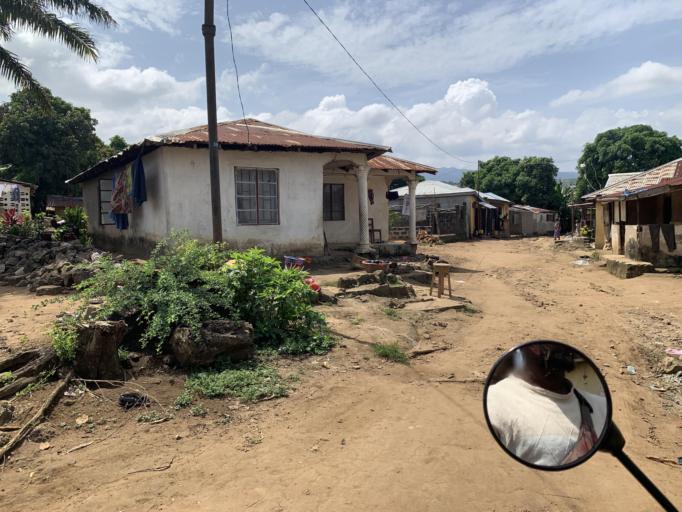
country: SL
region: Western Area
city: Hastings
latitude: 8.4104
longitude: -13.1340
